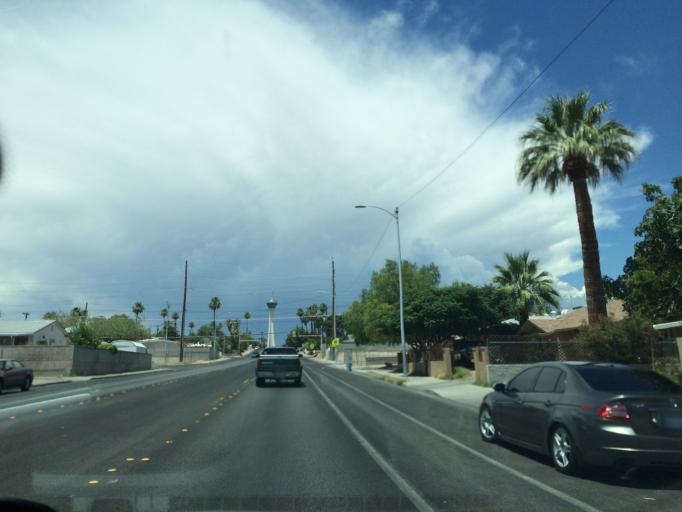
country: US
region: Nevada
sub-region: Clark County
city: Winchester
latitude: 36.1481
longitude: -115.1267
